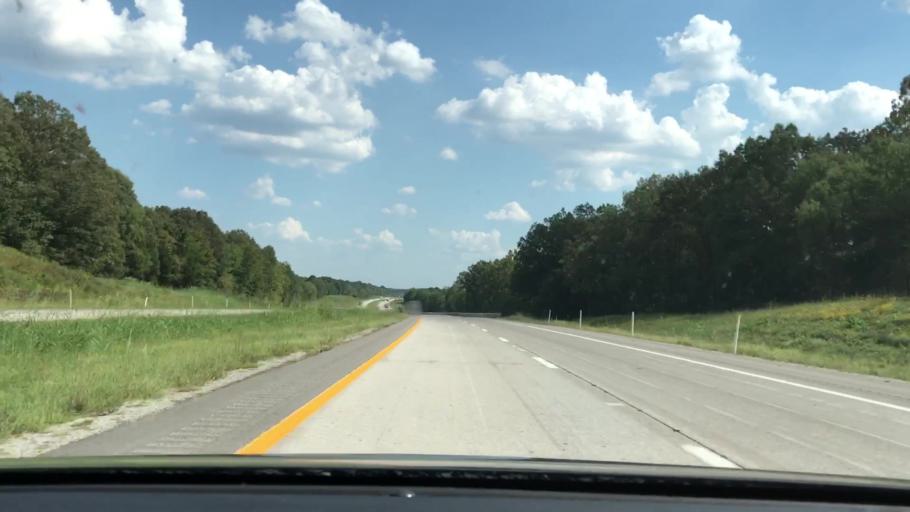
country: US
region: Kentucky
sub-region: Ohio County
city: Oak Grove
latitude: 37.3492
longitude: -86.7826
